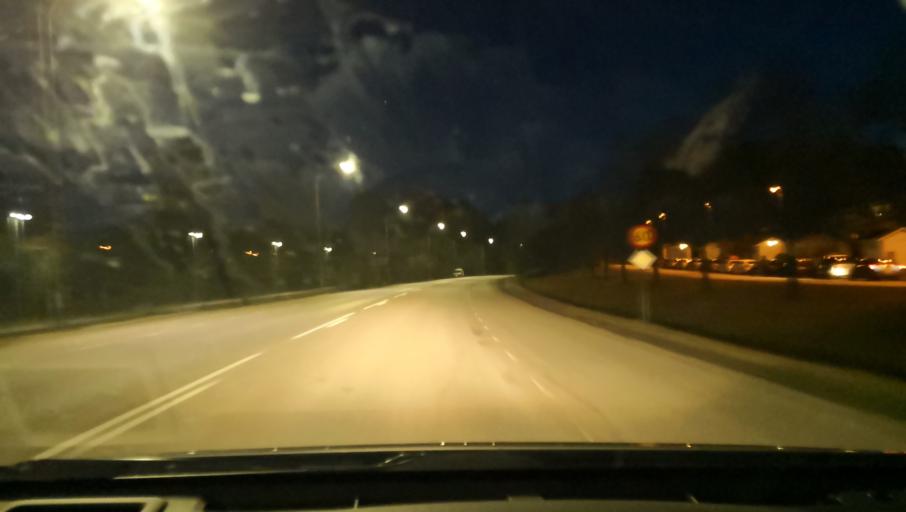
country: SE
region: Vaestmanland
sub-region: Vasteras
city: Vasteras
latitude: 59.6070
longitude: 16.5994
